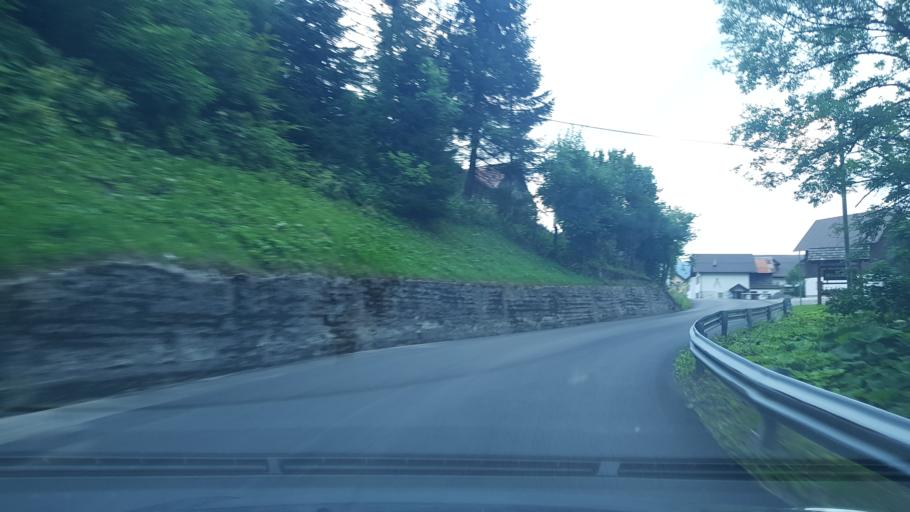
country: IT
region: Friuli Venezia Giulia
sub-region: Provincia di Udine
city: Forni Avoltri
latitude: 46.5819
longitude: 12.7961
